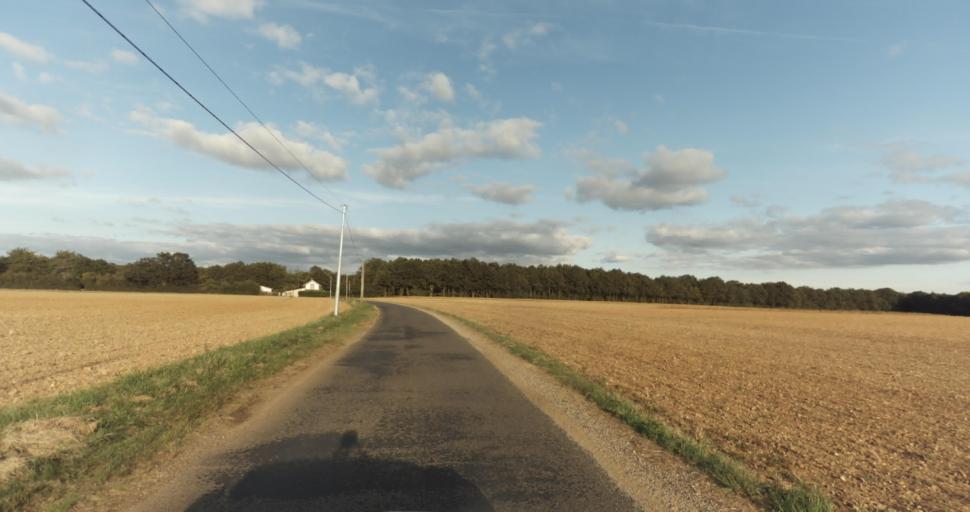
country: FR
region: Haute-Normandie
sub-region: Departement de l'Eure
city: Marcilly-sur-Eure
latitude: 48.8808
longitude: 1.2761
